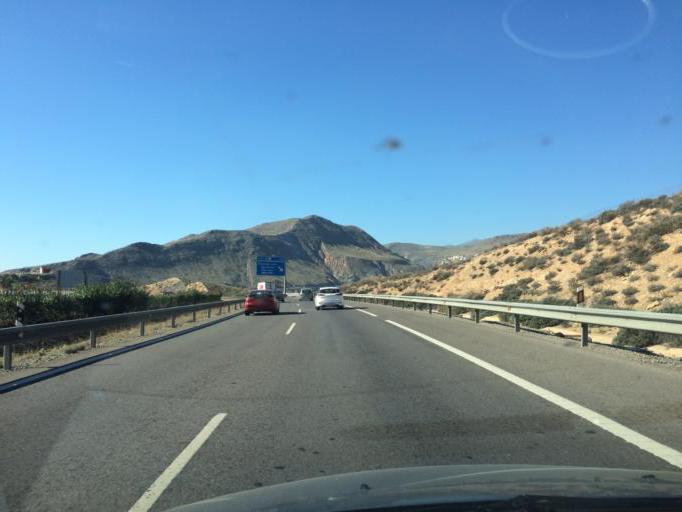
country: ES
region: Andalusia
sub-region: Provincia de Almeria
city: Aguadulce
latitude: 36.8276
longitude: -2.5861
